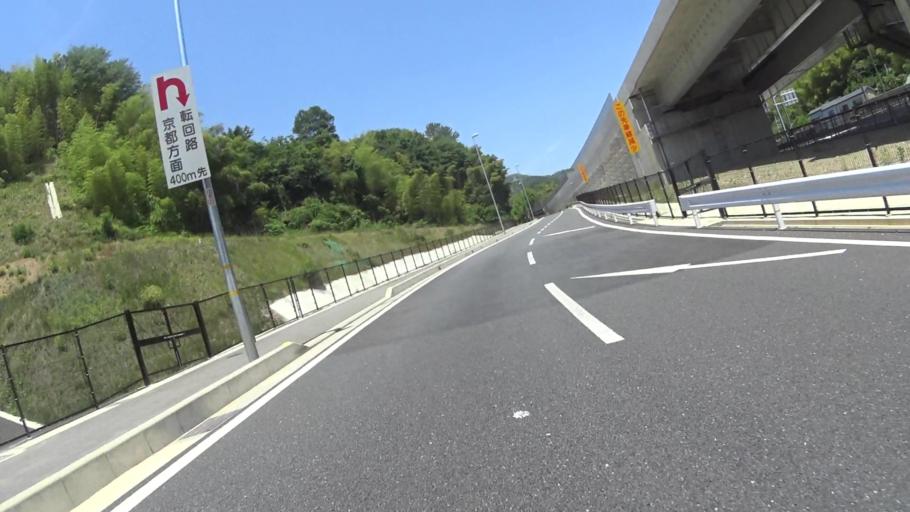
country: JP
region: Kyoto
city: Muko
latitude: 34.9773
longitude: 135.6583
